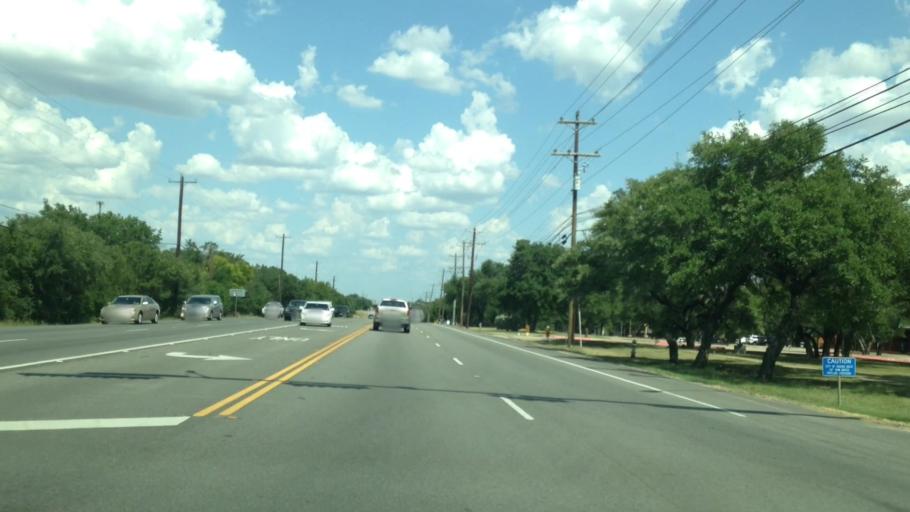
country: US
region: Texas
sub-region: Williamson County
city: Georgetown
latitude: 30.6327
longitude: -97.7103
